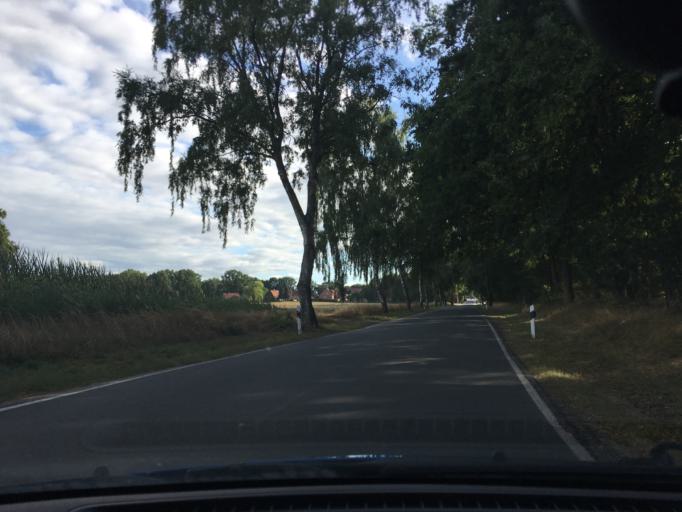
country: DE
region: Lower Saxony
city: Stelle
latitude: 53.3358
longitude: 10.0824
